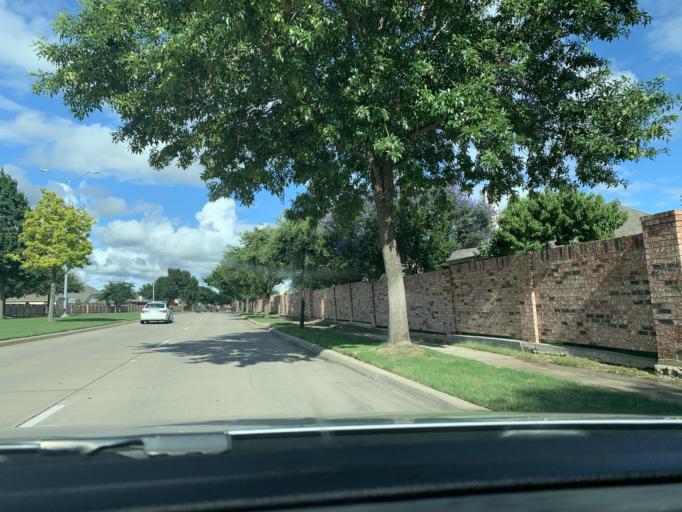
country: US
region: Texas
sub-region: Dallas County
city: Cedar Hill
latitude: 32.6456
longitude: -97.0246
